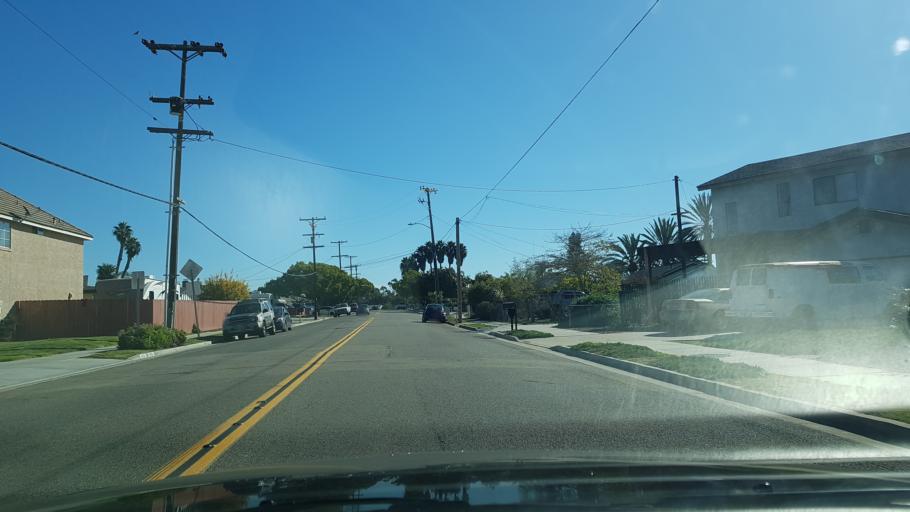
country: US
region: California
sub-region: San Diego County
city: Oceanside
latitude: 33.2057
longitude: -117.3535
